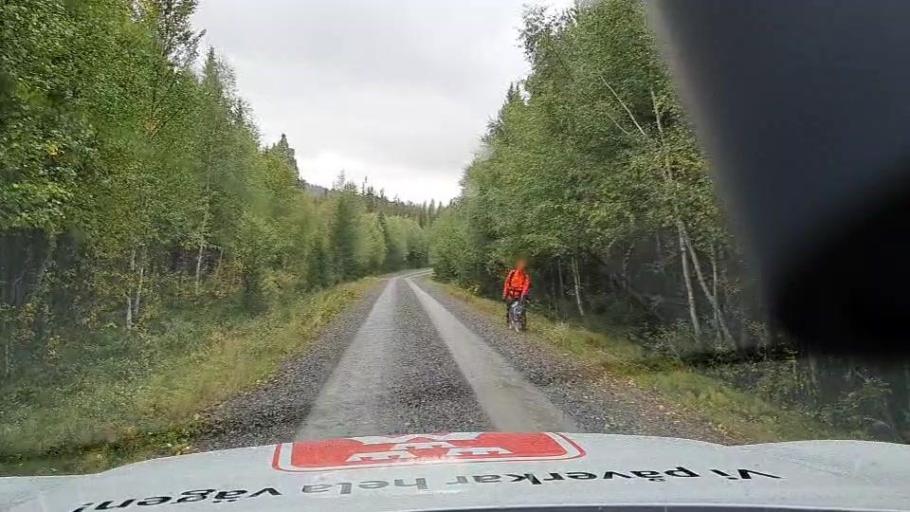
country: SE
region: Jaemtland
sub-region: Are Kommun
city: Jarpen
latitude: 63.1937
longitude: 13.2623
